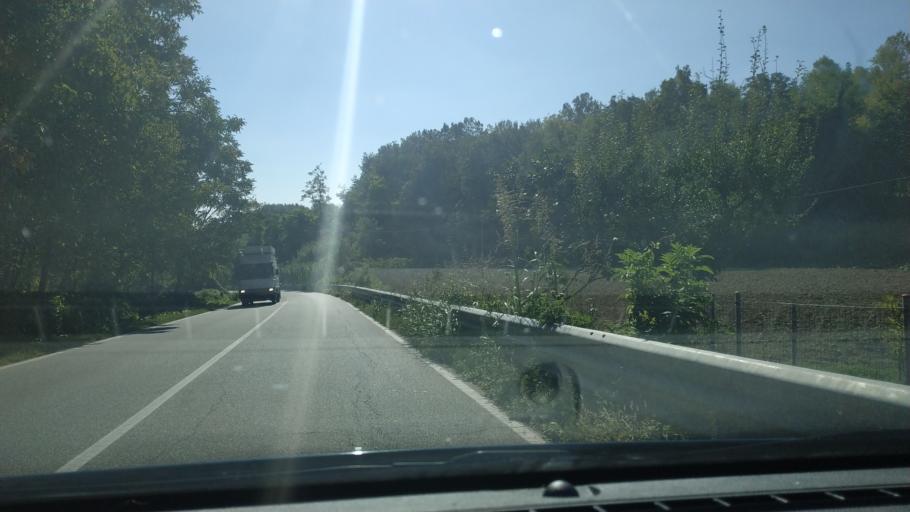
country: IT
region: Piedmont
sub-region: Provincia di Alessandria
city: Ozzano Monferrato
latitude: 45.1080
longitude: 8.3878
